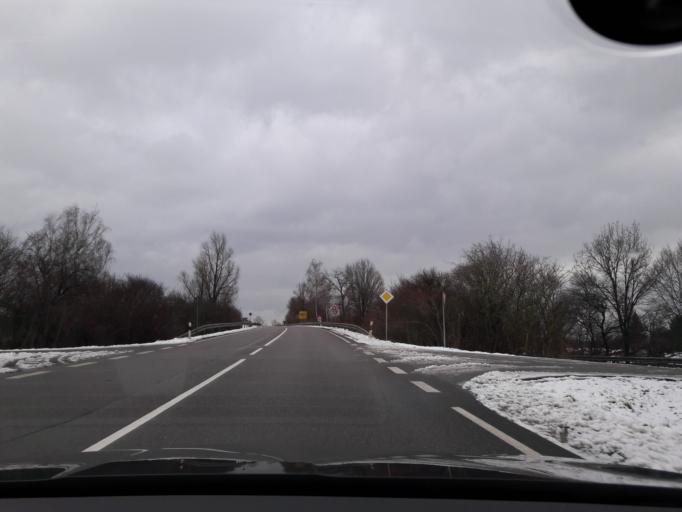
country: DE
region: Bavaria
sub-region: Upper Bavaria
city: Karlsfeld
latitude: 48.2498
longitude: 11.4743
